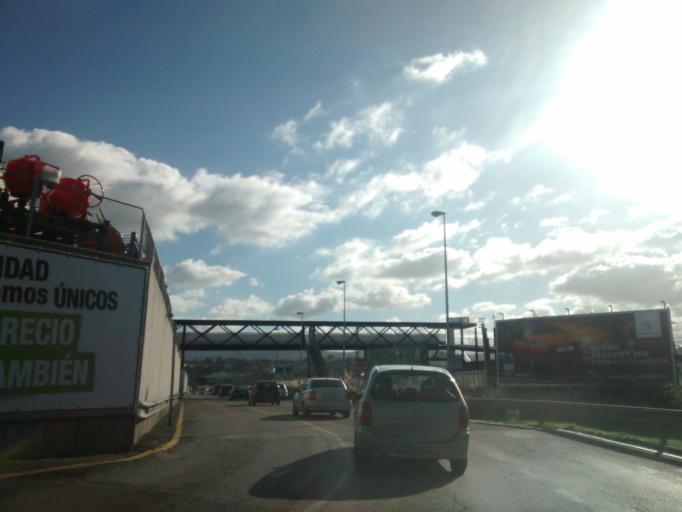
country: ES
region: Cantabria
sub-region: Provincia de Cantabria
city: El Astillero
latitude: 43.4282
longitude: -3.8406
